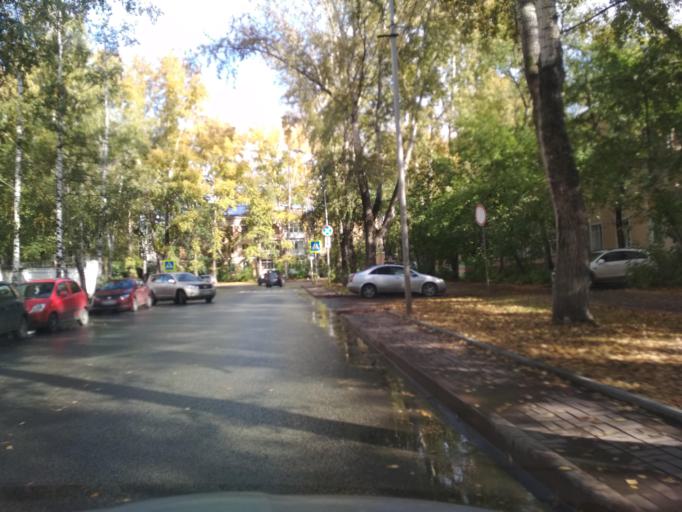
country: RU
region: Tomsk
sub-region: Tomskiy Rayon
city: Tomsk
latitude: 56.4637
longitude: 84.9800
